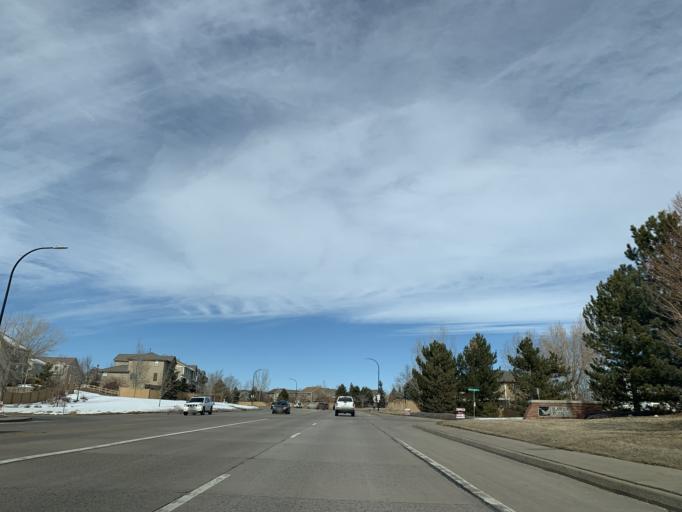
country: US
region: Colorado
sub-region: Douglas County
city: Carriage Club
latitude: 39.5243
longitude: -104.9338
